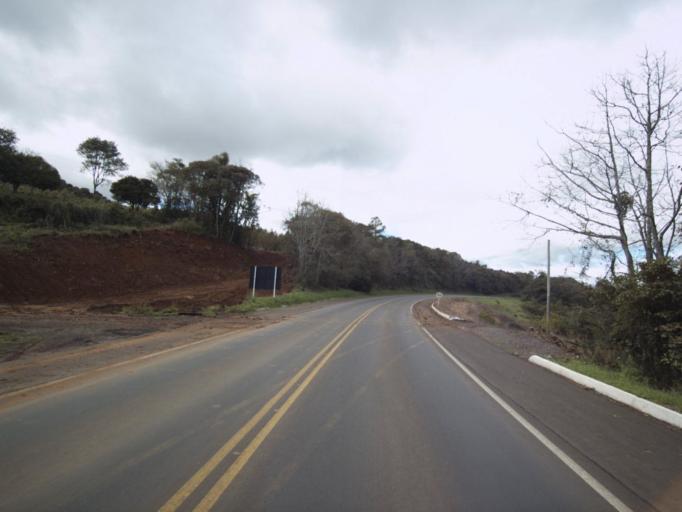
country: BR
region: Santa Catarina
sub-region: Concordia
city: Concordia
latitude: -27.3189
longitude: -51.9844
